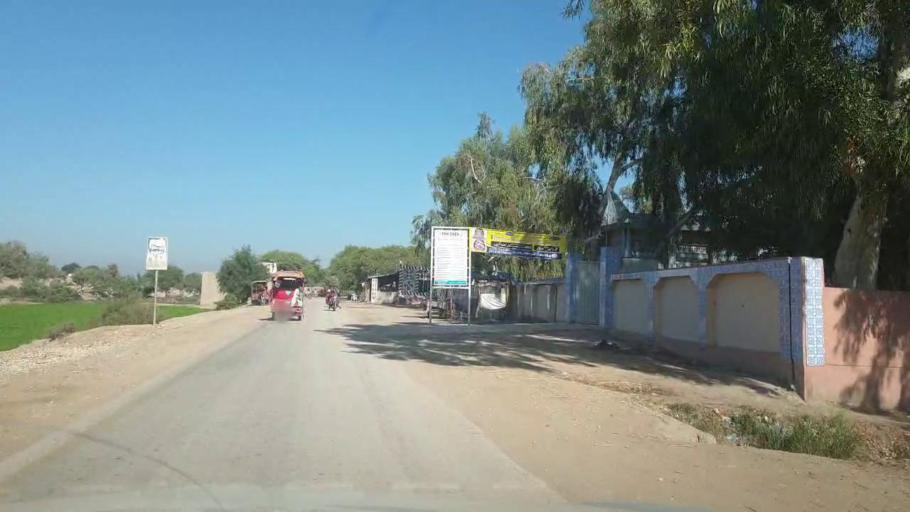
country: PK
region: Sindh
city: Bhan
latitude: 26.5472
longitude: 67.6340
